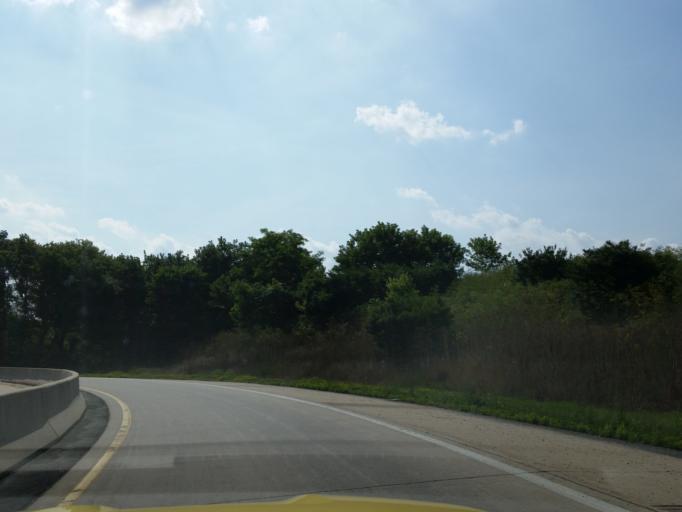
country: US
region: Pennsylvania
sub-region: Lancaster County
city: Lancaster
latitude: 40.0568
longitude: -76.2674
